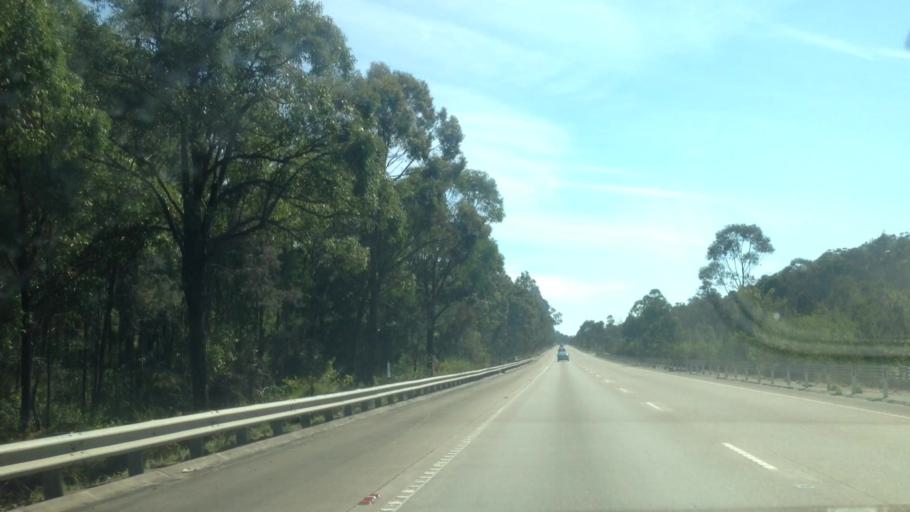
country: AU
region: New South Wales
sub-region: Lake Macquarie Shire
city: Fennell Bay
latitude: -32.9712
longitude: 151.5336
